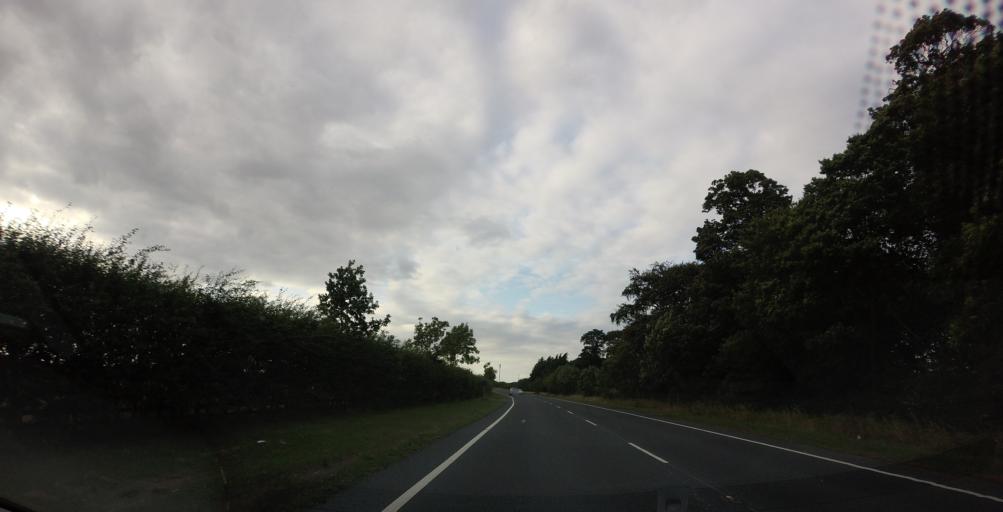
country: GB
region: England
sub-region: North Yorkshire
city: Boroughbridge
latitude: 54.0713
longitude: -1.3910
